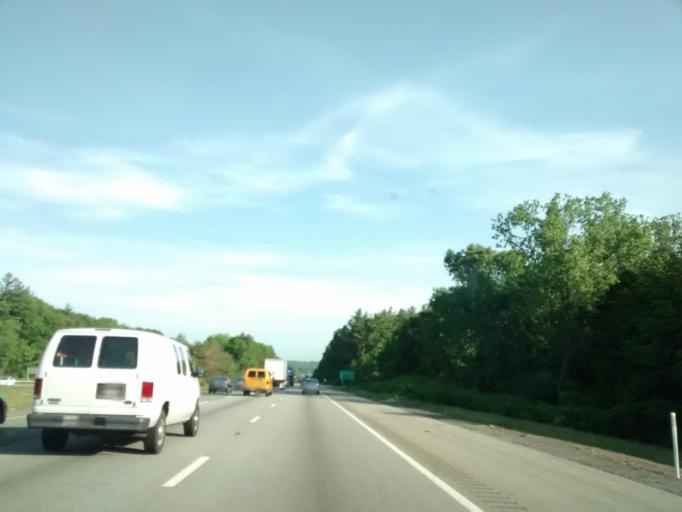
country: US
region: Massachusetts
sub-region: Worcester County
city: Berlin
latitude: 42.3845
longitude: -71.6033
